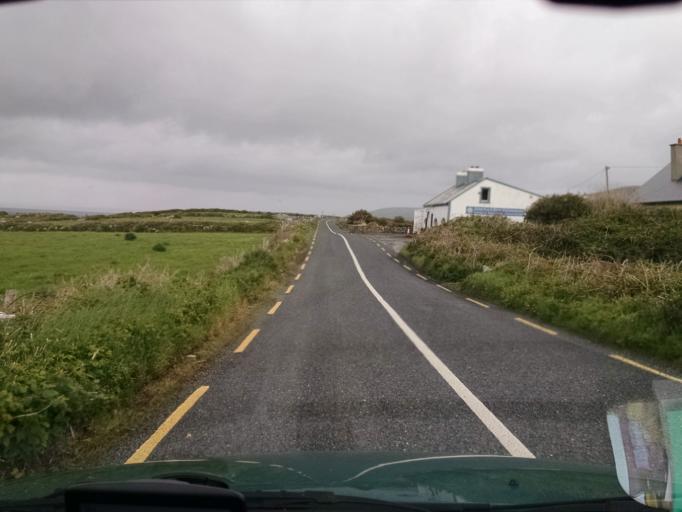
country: IE
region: Connaught
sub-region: County Galway
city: Bearna
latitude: 53.0941
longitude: -9.3059
